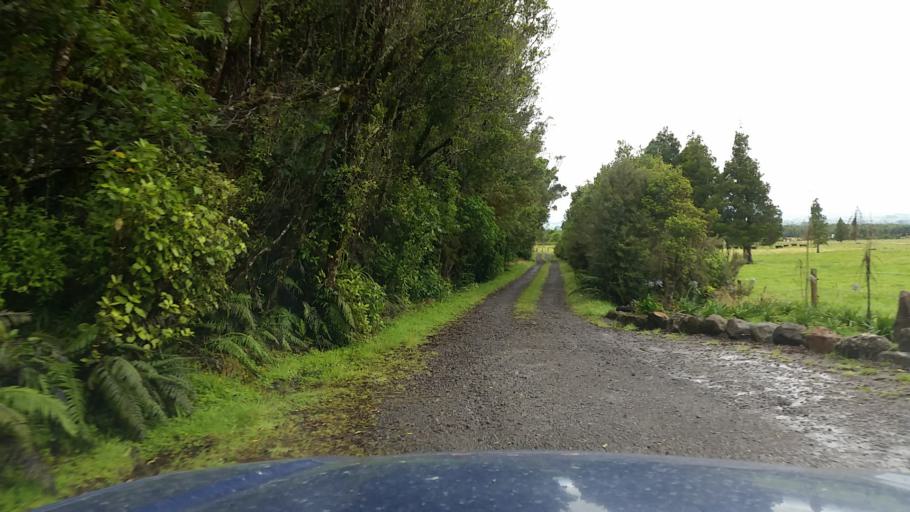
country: NZ
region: Taranaki
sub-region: South Taranaki District
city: Eltham
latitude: -39.2882
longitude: 174.1756
